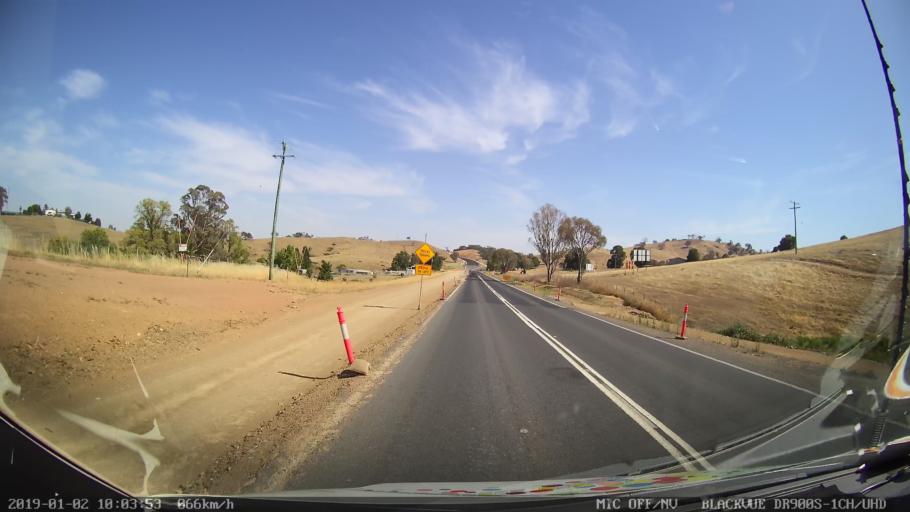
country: AU
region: New South Wales
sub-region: Gundagai
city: Gundagai
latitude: -35.1732
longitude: 148.1248
